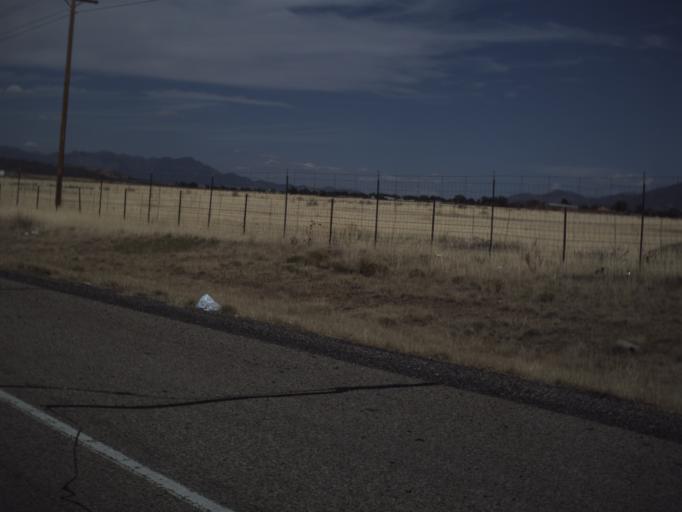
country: US
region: Utah
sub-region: Millard County
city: Fillmore
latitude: 38.9499
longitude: -112.3476
